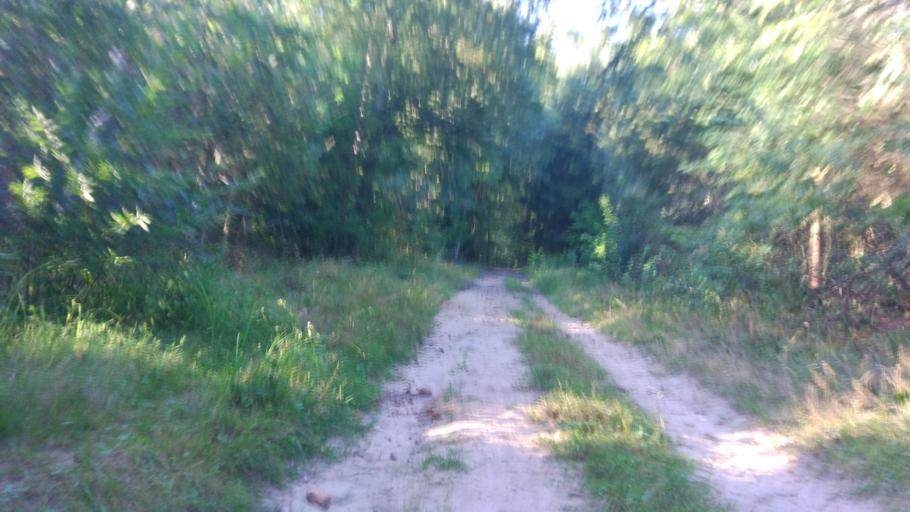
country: FR
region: Alsace
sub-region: Departement du Bas-Rhin
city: Gries
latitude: 48.7702
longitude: 7.8214
